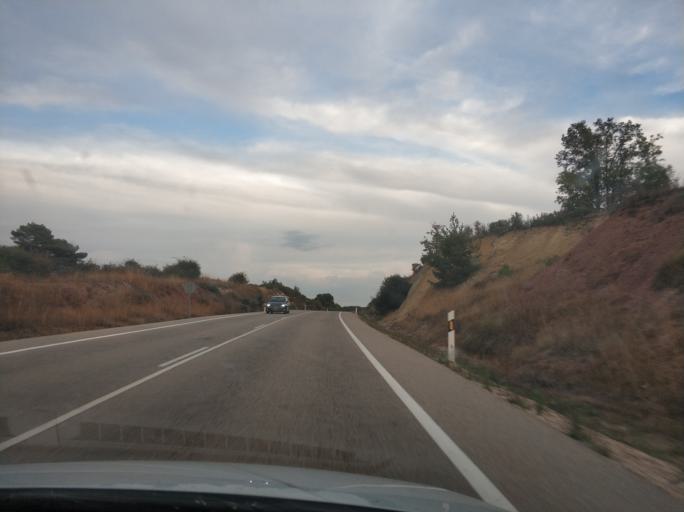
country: ES
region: Castille and Leon
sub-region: Provincia de Burgos
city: Cabezon de la Sierra
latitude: 41.8944
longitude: -3.2584
